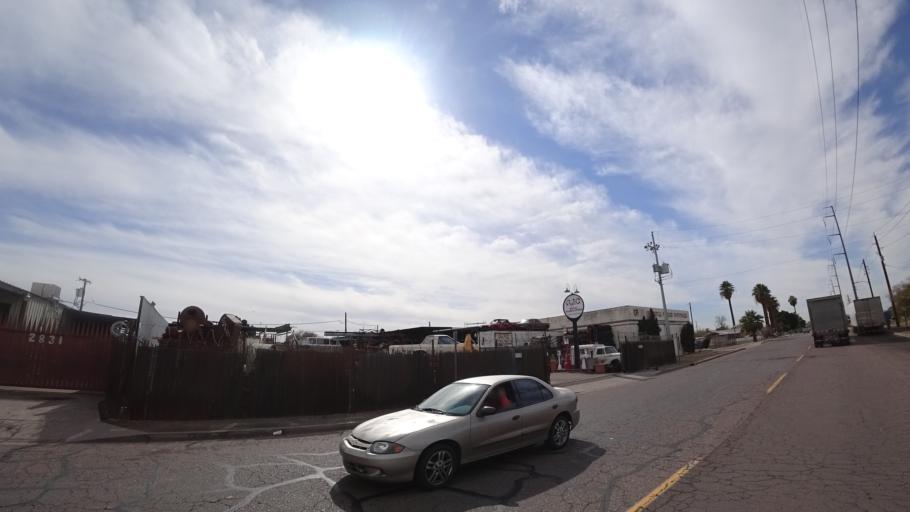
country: US
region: Arizona
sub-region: Maricopa County
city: Phoenix
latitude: 33.4732
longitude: -112.1203
